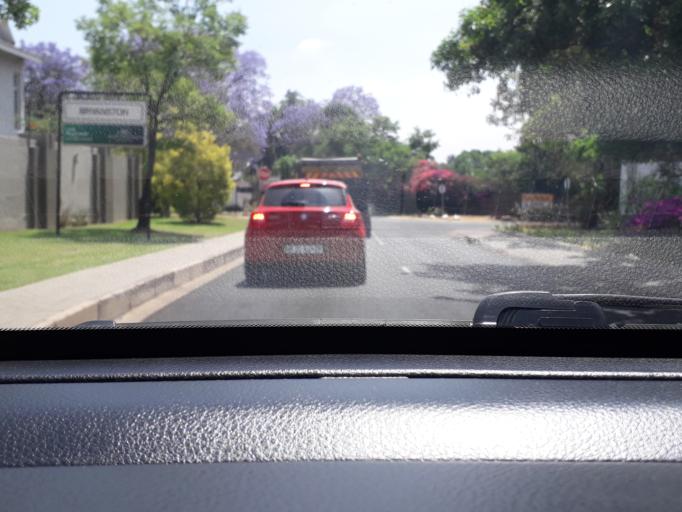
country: ZA
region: Gauteng
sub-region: City of Johannesburg Metropolitan Municipality
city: Midrand
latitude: -26.0391
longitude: 28.0352
